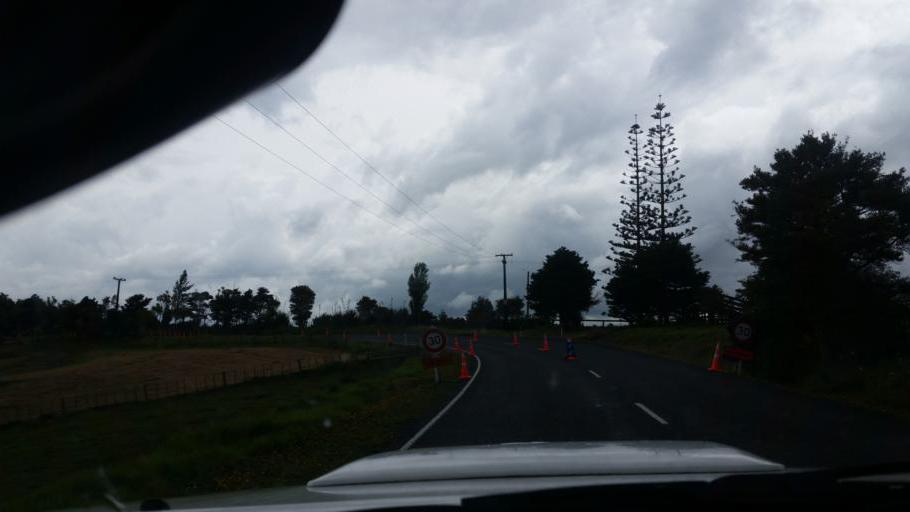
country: NZ
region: Auckland
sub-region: Auckland
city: Wellsford
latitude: -36.1467
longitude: 174.2236
